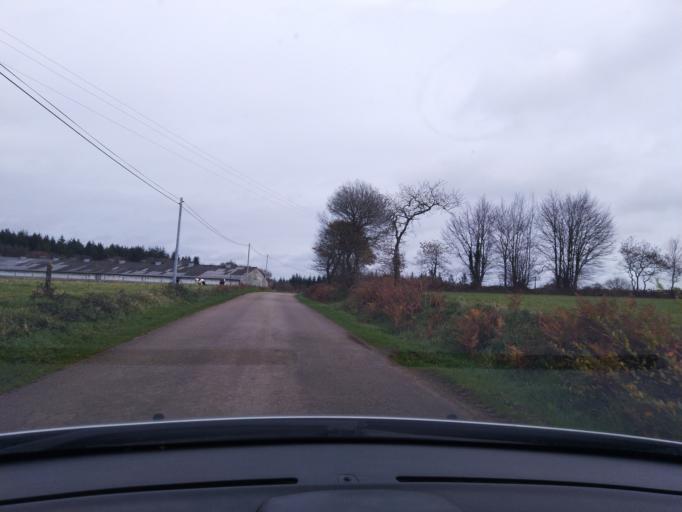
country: FR
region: Brittany
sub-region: Departement du Finistere
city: Guerlesquin
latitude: 48.5367
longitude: -3.5618
